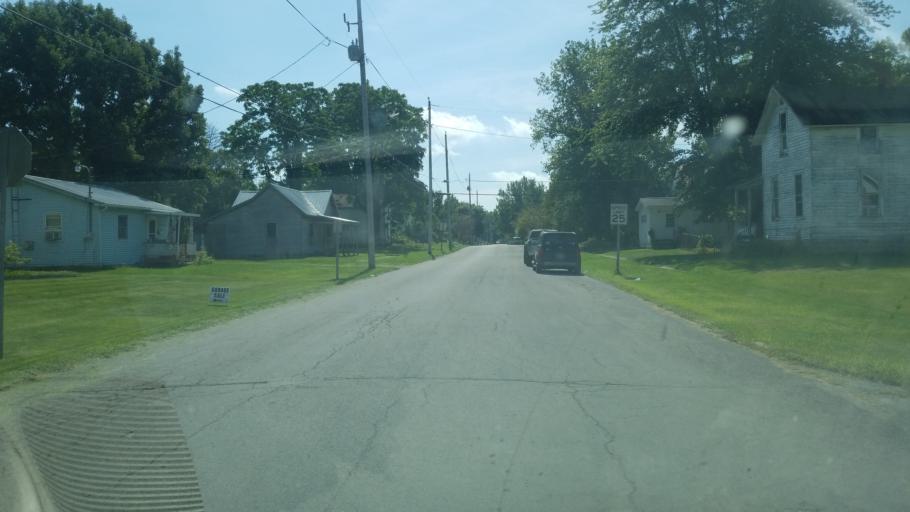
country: US
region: Ohio
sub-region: Hardin County
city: Kenton
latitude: 40.6425
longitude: -83.6064
